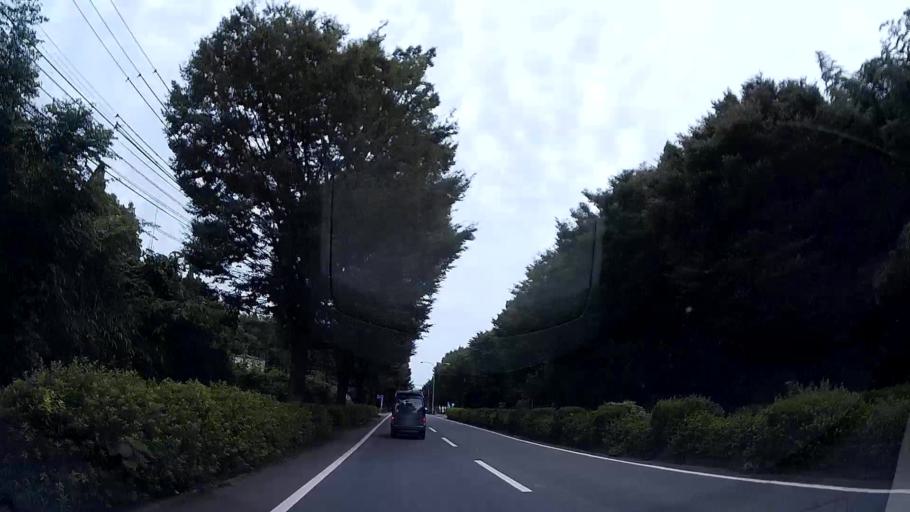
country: JP
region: Kumamoto
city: Ozu
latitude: 32.8953
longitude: 130.8539
